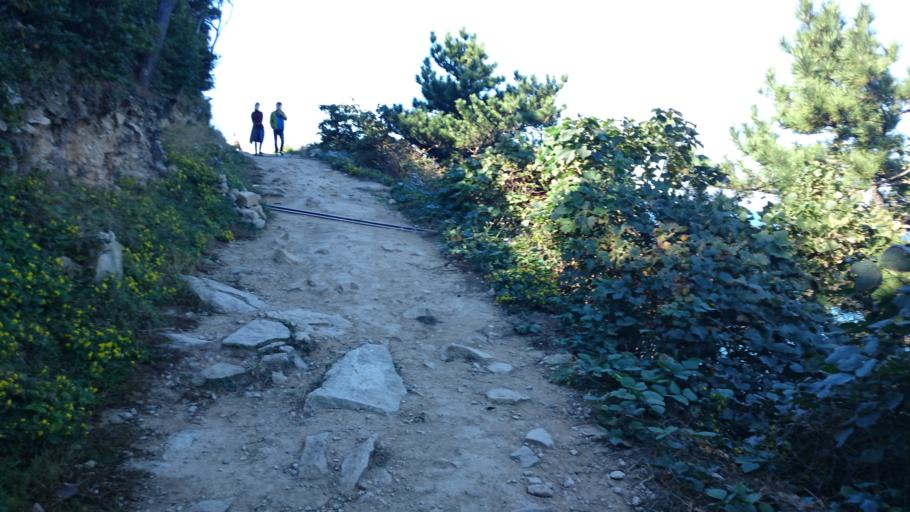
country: KR
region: Gyeongsangnam-do
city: Kyosai
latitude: 34.6298
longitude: 128.5493
